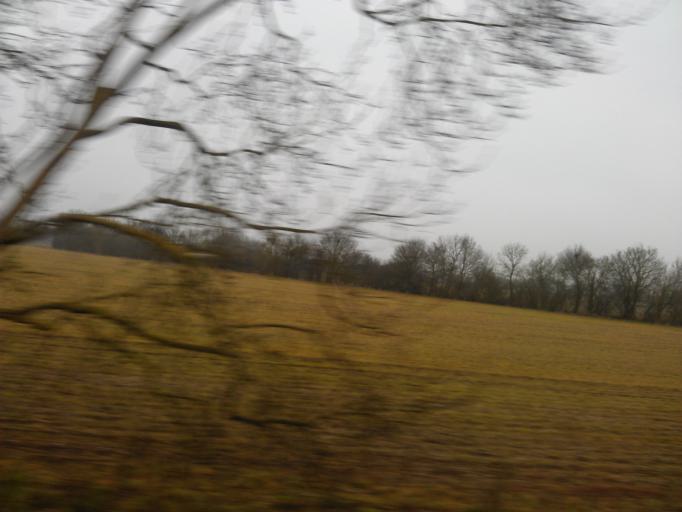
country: GB
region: England
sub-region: Essex
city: Marks Tey
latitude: 51.8682
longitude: 0.7578
